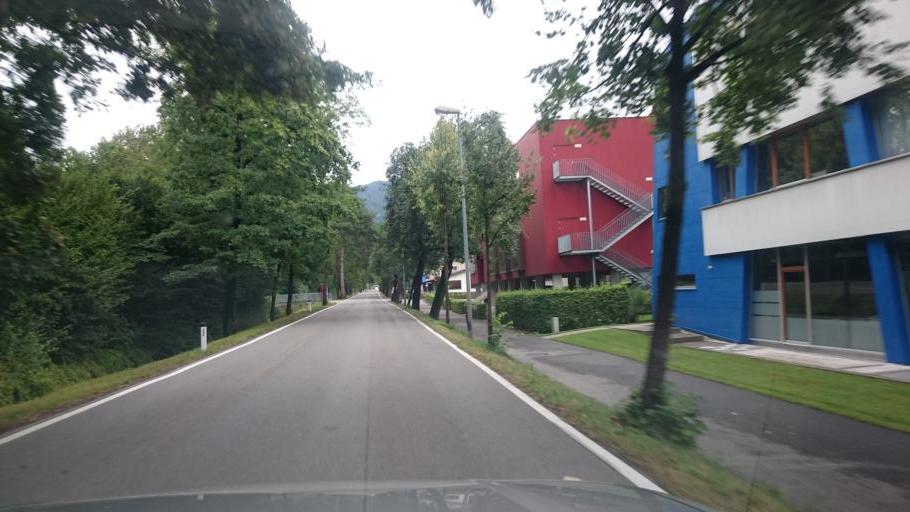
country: AT
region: Vorarlberg
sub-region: Politischer Bezirk Dornbirn
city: Dornbirn
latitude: 47.4343
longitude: 9.7407
